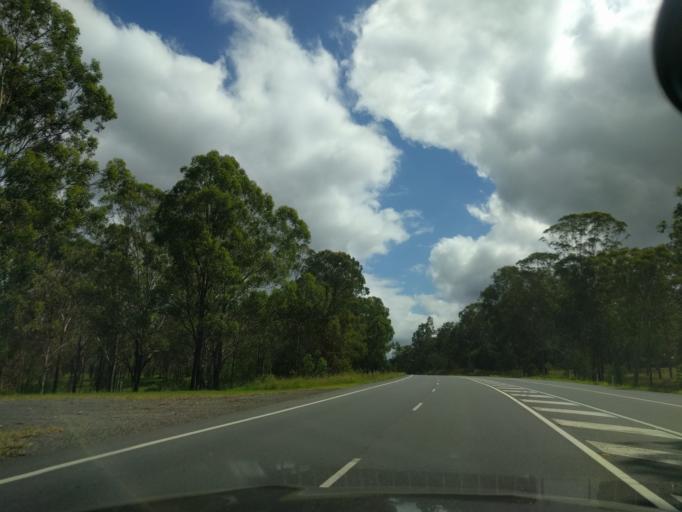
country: AU
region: Queensland
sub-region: Logan
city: Cedar Vale
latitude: -27.8798
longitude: 152.9884
